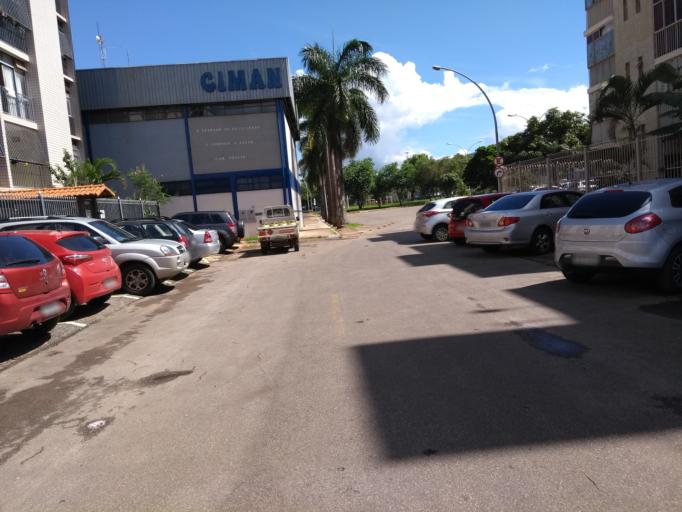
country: BR
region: Federal District
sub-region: Brasilia
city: Brasilia
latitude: -15.8003
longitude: -47.9419
